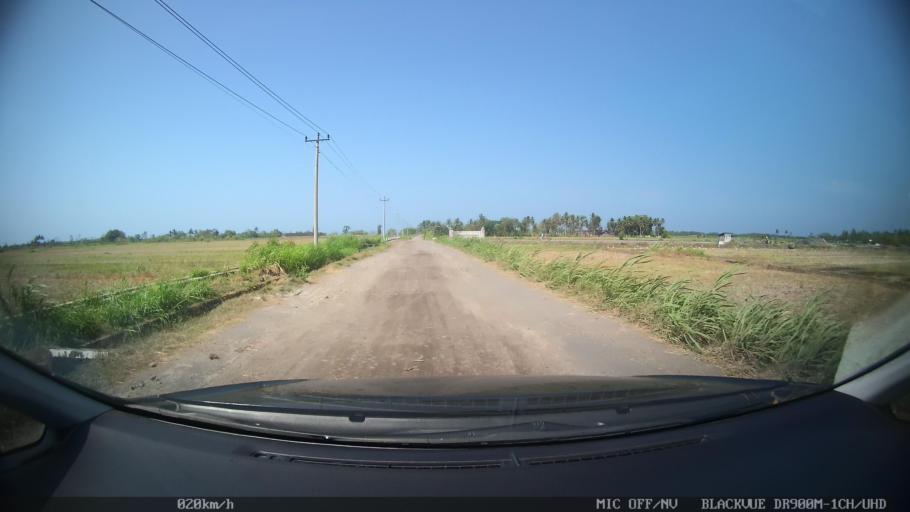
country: ID
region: Daerah Istimewa Yogyakarta
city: Srandakan
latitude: -7.9713
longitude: 110.2112
